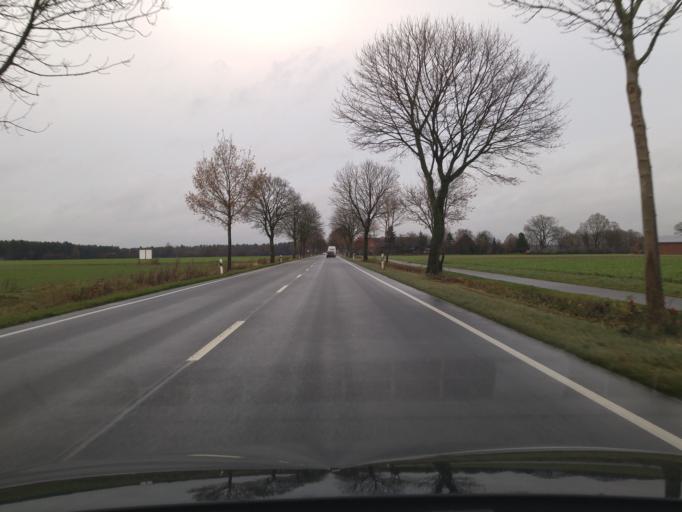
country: DE
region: Lower Saxony
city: Gross Oesingen
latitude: 52.6633
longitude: 10.4663
